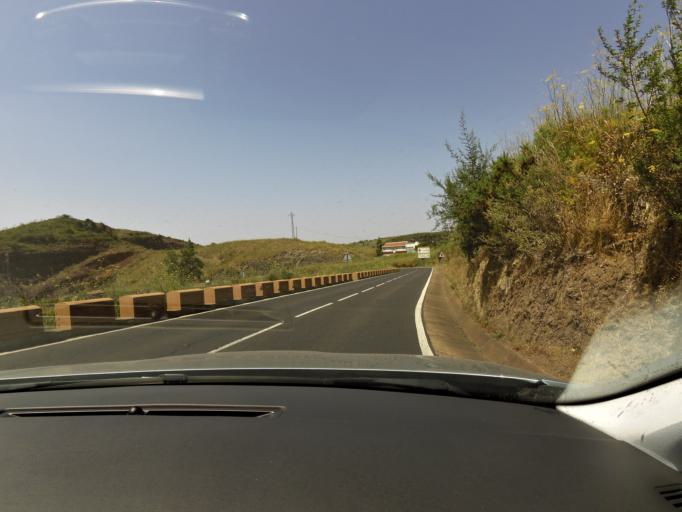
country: ES
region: Canary Islands
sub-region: Provincia de Santa Cruz de Tenerife
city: Santiago del Teide
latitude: 28.3166
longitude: -16.8047
